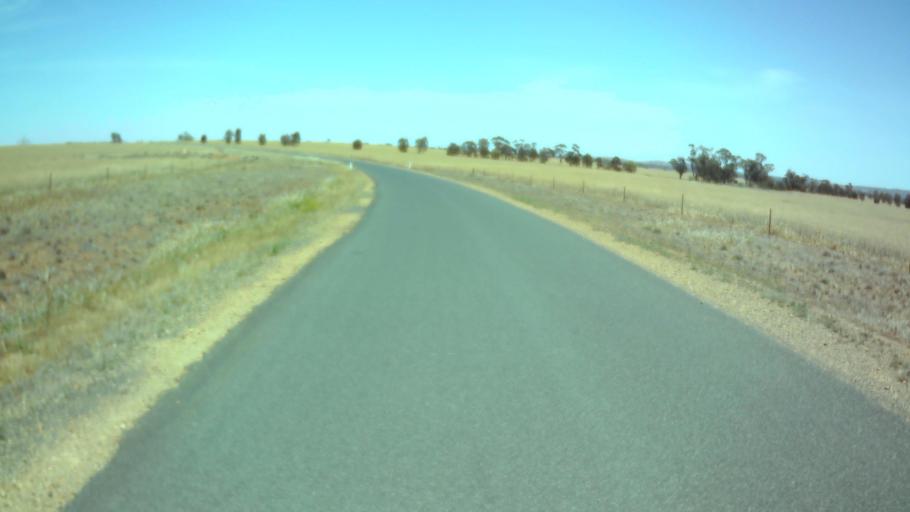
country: AU
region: New South Wales
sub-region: Weddin
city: Grenfell
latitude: -33.8550
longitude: 147.9354
